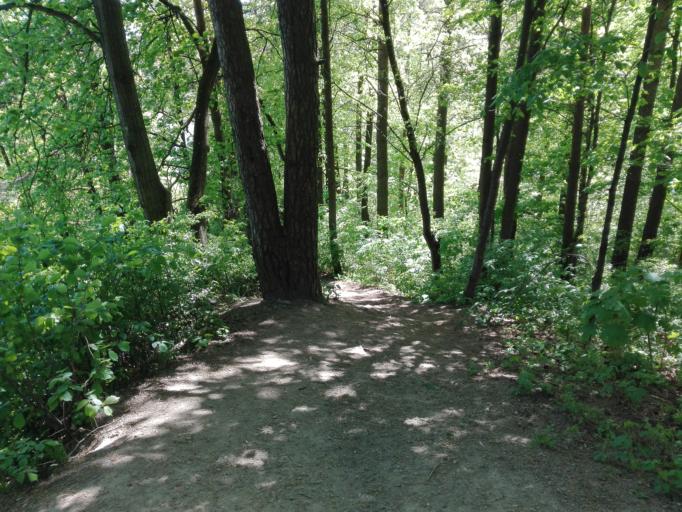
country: LT
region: Vilnius County
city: Lazdynai
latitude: 54.6884
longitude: 25.2252
